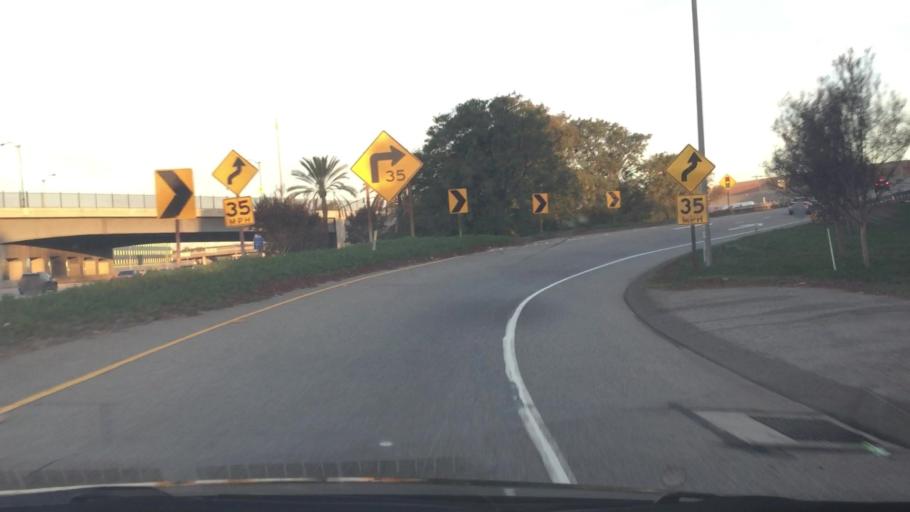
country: US
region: California
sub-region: Orange County
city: Anaheim
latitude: 33.8148
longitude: -117.9141
